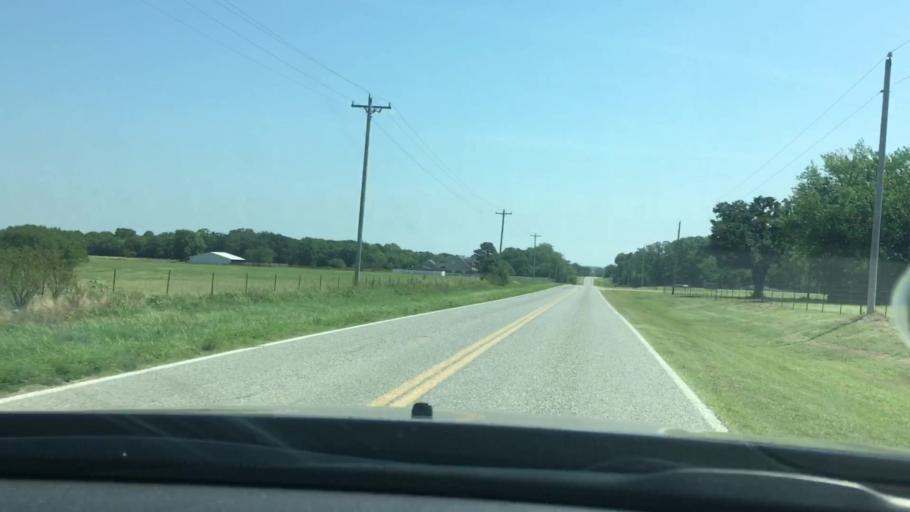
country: US
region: Oklahoma
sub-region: Johnston County
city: Tishomingo
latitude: 34.2741
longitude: -96.5043
